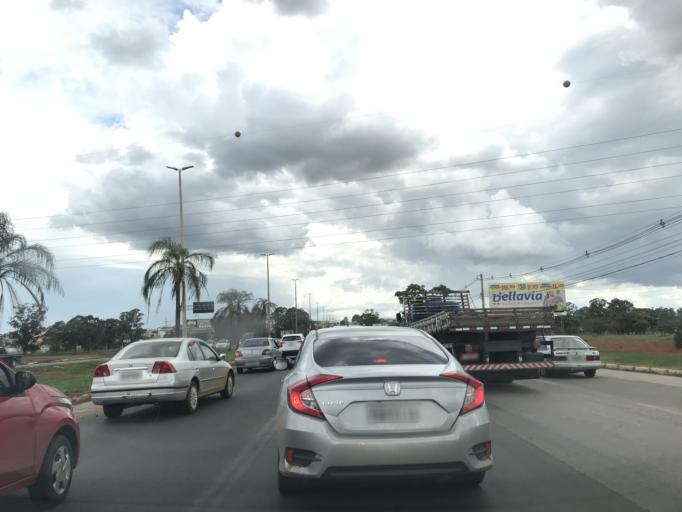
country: BR
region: Federal District
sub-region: Brasilia
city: Brasilia
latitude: -15.8856
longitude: -48.0598
